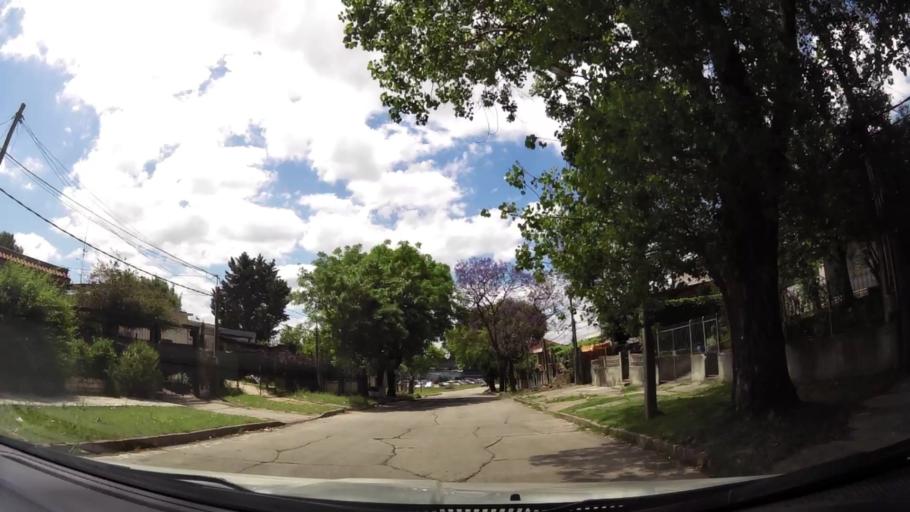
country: UY
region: Montevideo
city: Montevideo
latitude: -34.8501
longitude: -56.2342
